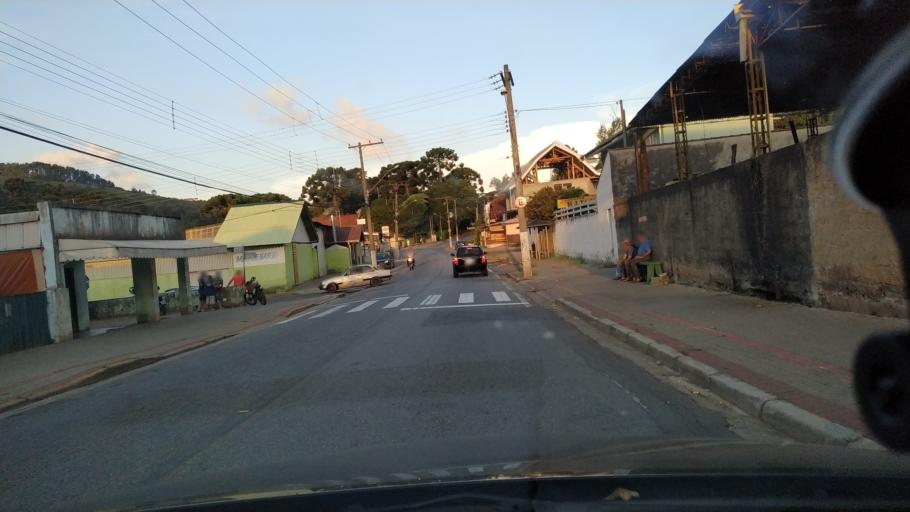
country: BR
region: Sao Paulo
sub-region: Campos Do Jordao
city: Campos do Jordao
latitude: -22.7459
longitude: -45.6167
